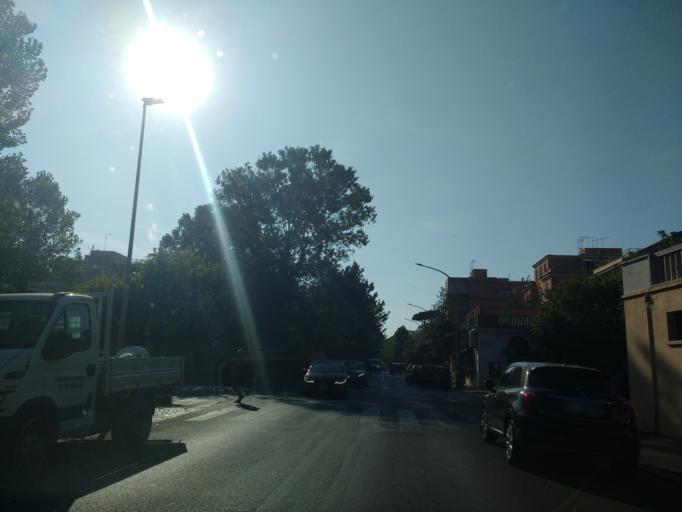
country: IT
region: Latium
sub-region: Citta metropolitana di Roma Capitale
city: Lido di Ostia
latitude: 41.7294
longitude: 12.2848
